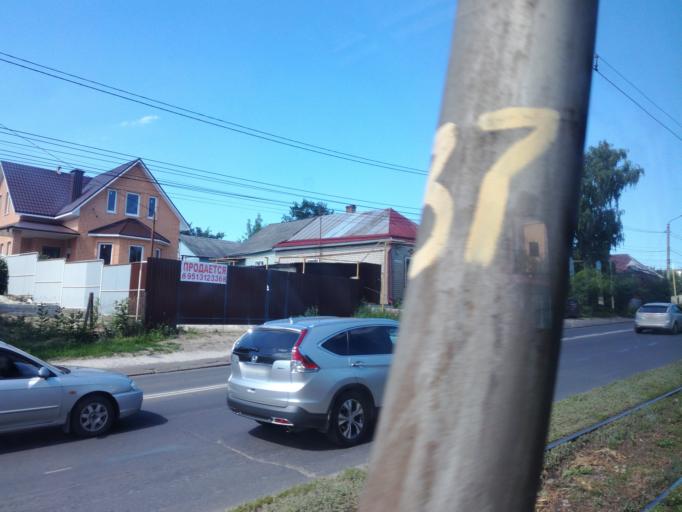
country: RU
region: Kursk
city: Kursk
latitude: 51.7515
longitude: 36.1781
